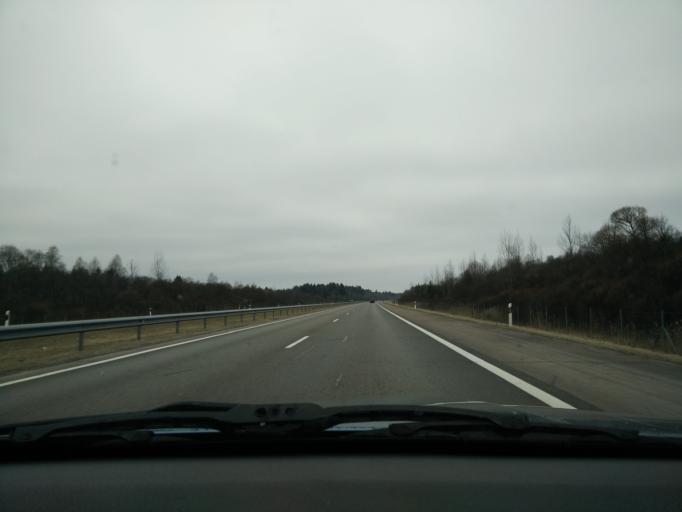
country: LT
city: Rietavas
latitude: 55.6111
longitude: 22.0424
